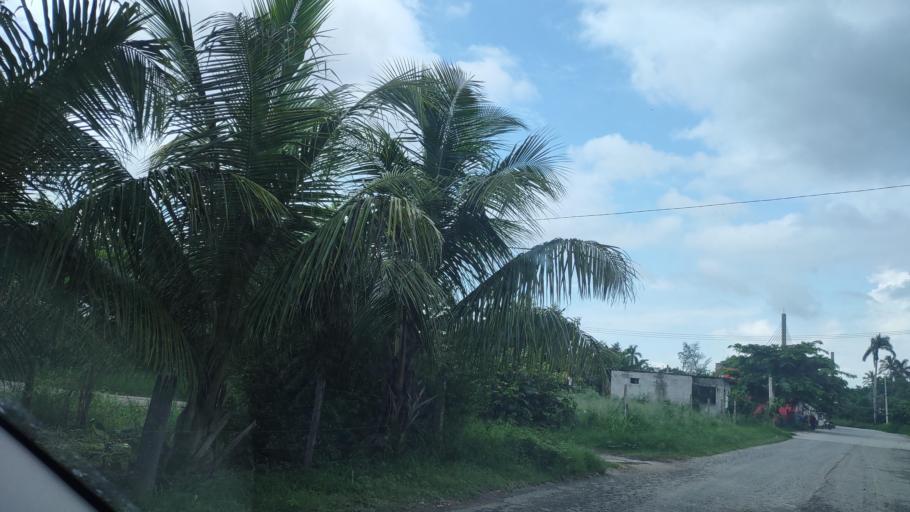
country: MX
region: Veracruz
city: Anahuac
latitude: 22.2245
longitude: -97.8293
